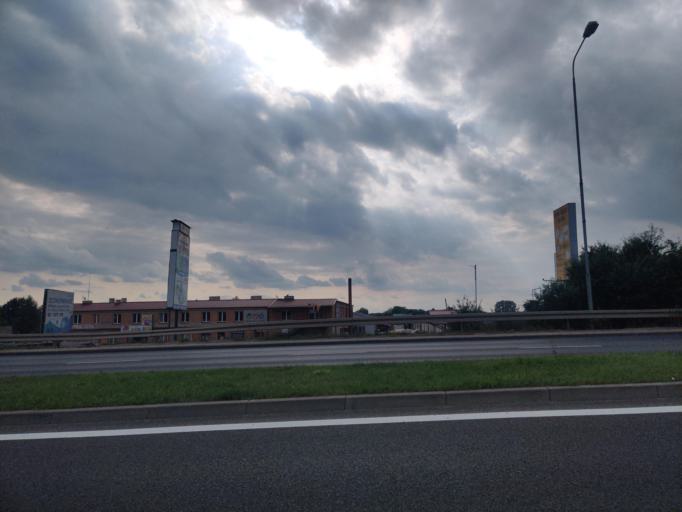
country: PL
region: Greater Poland Voivodeship
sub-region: Konin
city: Konin
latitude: 52.2193
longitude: 18.2526
